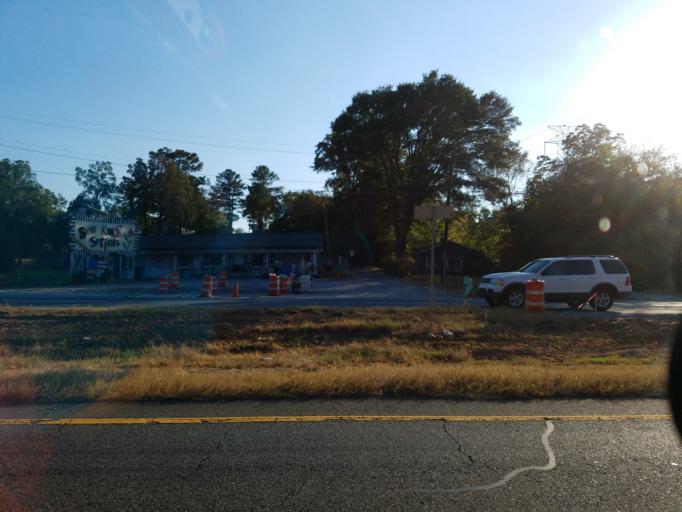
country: US
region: Georgia
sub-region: Bartow County
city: Cartersville
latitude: 34.2026
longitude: -84.8048
